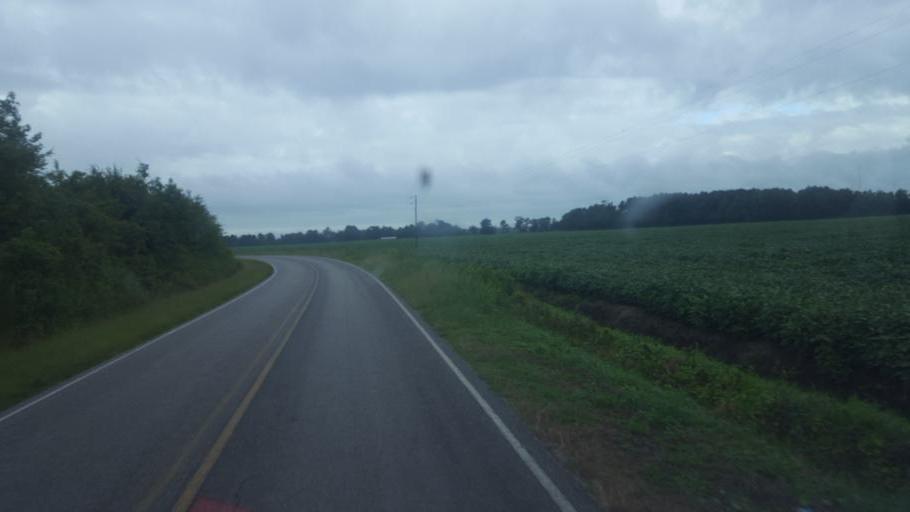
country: US
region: North Carolina
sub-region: Tyrrell County
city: Columbia
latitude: 35.9442
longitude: -76.2820
